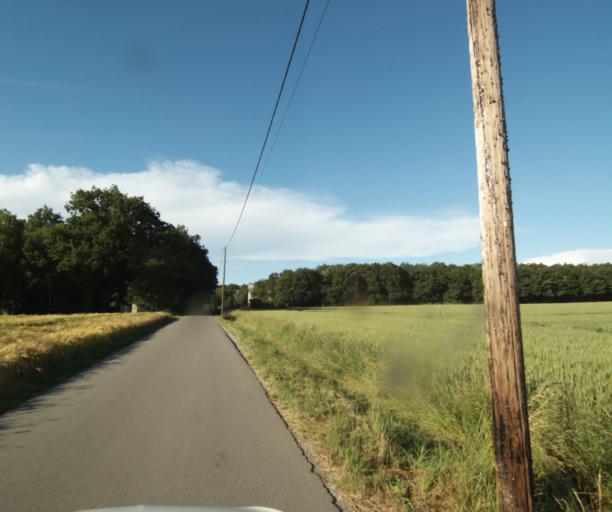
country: FR
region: Rhone-Alpes
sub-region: Departement de la Haute-Savoie
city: Loisin
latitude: 46.2705
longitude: 6.2911
